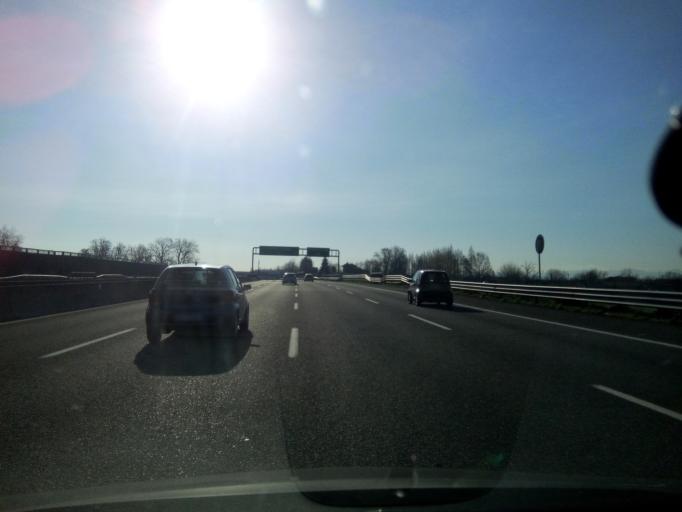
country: IT
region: Emilia-Romagna
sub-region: Provincia di Modena
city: San Damaso
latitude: 44.5819
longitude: 10.9703
